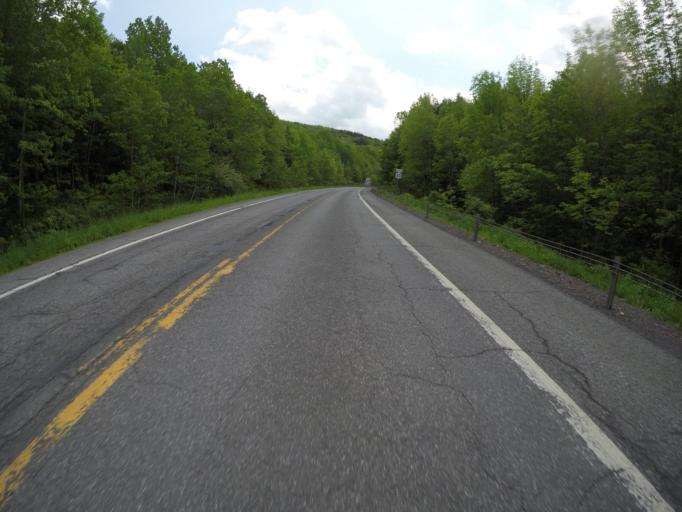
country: US
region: New York
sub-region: Delaware County
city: Stamford
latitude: 42.2129
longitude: -74.5931
